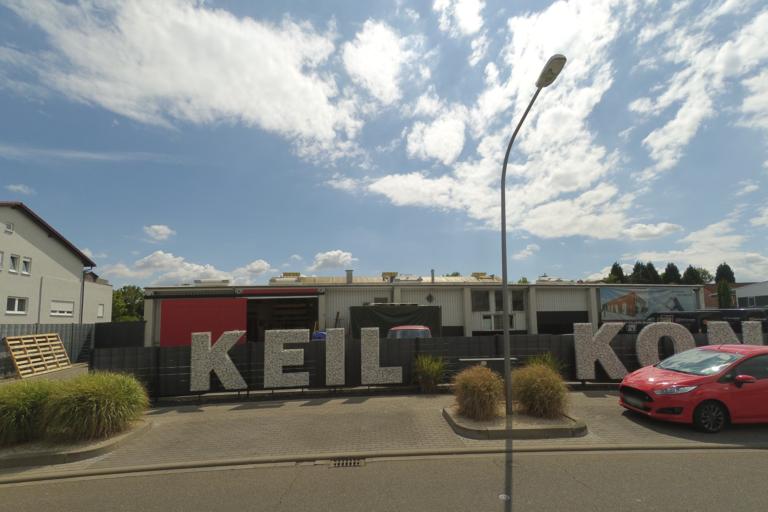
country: DE
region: Rheinland-Pfalz
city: Gartenstadt
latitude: 49.4504
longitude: 8.4213
